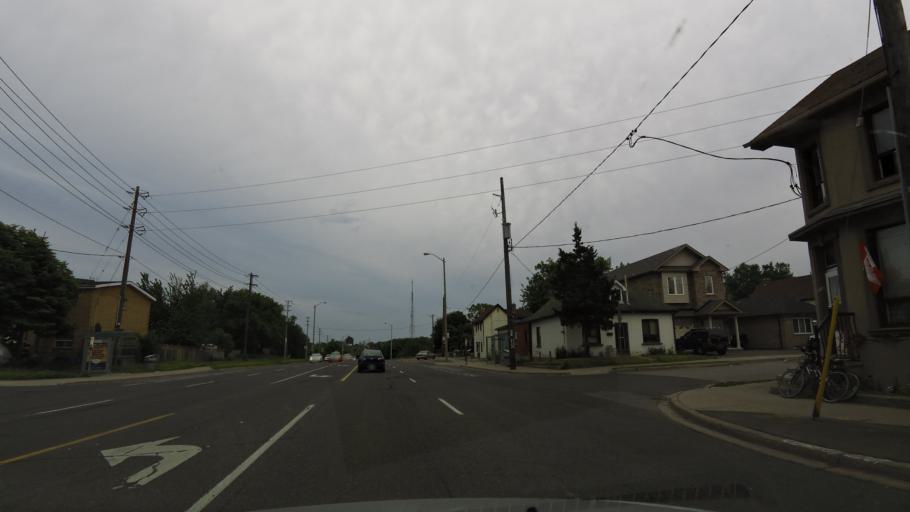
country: CA
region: Ontario
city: Etobicoke
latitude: 43.6895
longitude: -79.5005
